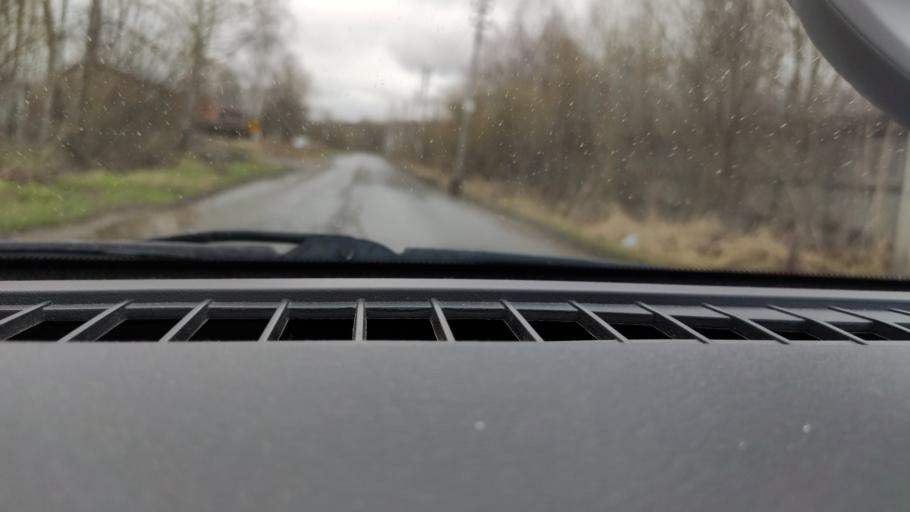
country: RU
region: Perm
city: Perm
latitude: 58.1056
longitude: 56.3556
